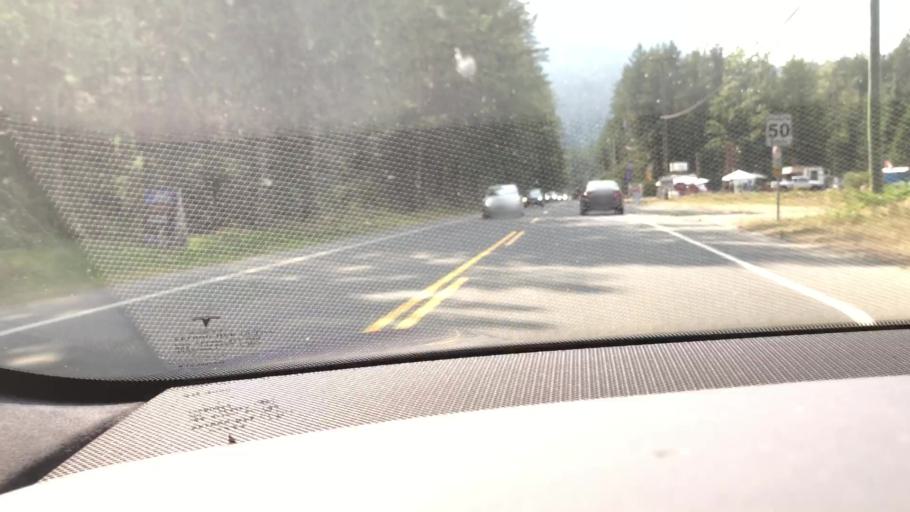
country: CA
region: British Columbia
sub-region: Fraser Valley Regional District
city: Chilliwack
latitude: 49.0751
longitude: -121.9684
